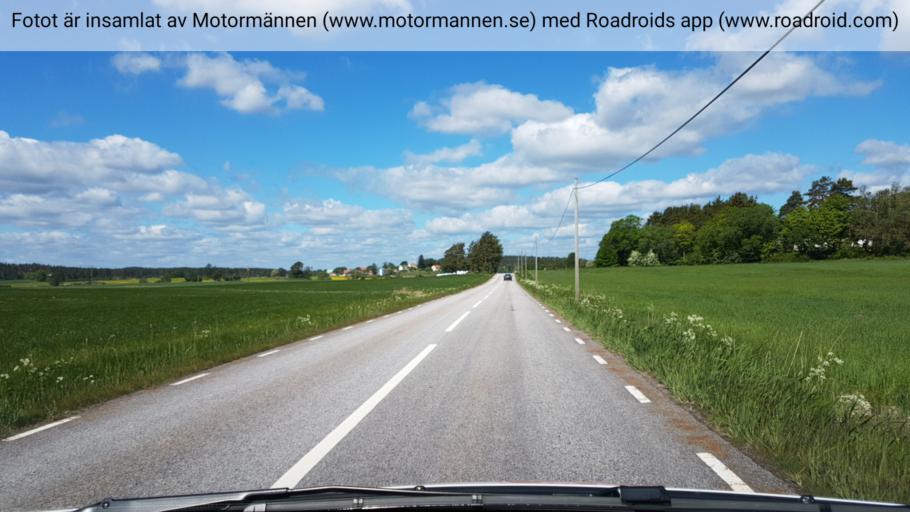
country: SE
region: Kalmar
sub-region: Vasterviks Kommun
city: Forserum
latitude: 57.9300
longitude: 16.5202
